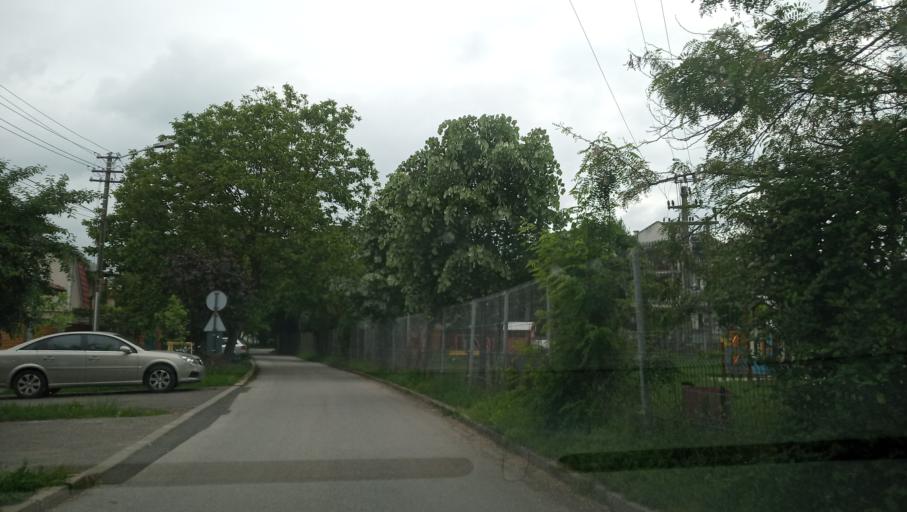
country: RO
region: Timis
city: Timisoara
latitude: 45.7531
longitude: 21.2622
